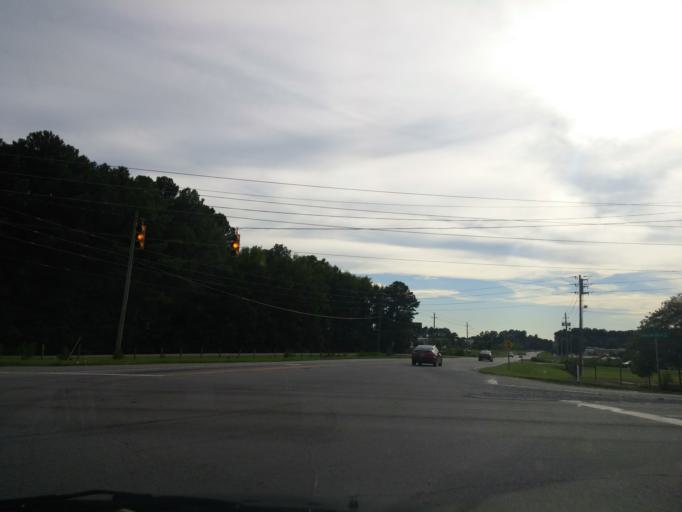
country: US
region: North Carolina
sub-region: Pitt County
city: Greenville
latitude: 35.6534
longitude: -77.3475
